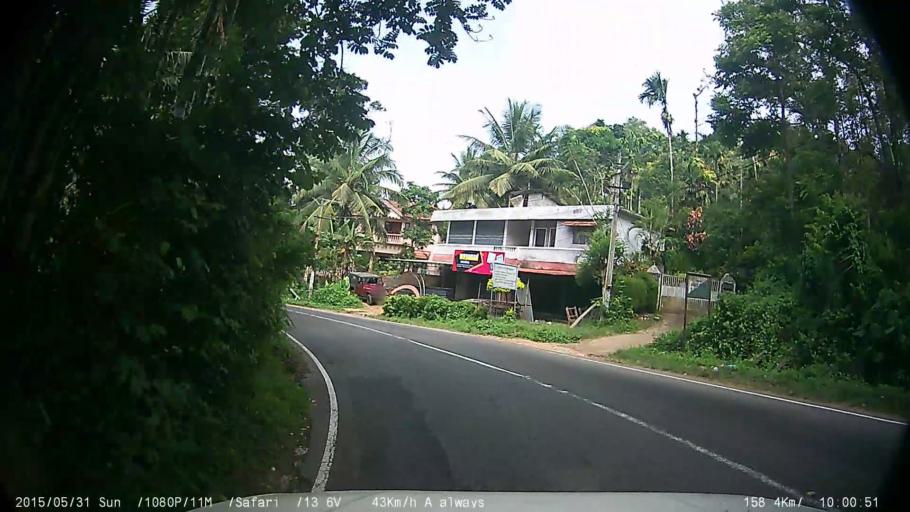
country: IN
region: Kerala
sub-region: Wayanad
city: Kalpetta
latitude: 11.5834
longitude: 76.0632
